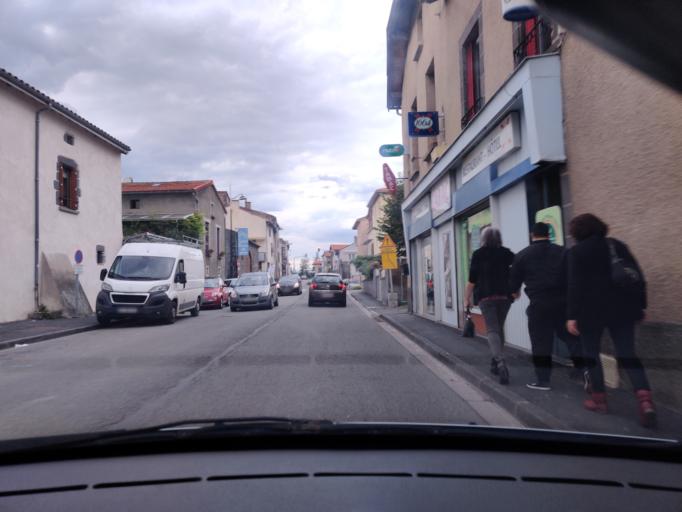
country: FR
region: Auvergne
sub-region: Departement du Puy-de-Dome
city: Saint-Bonnet-pres-Riom
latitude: 45.9290
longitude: 3.1127
